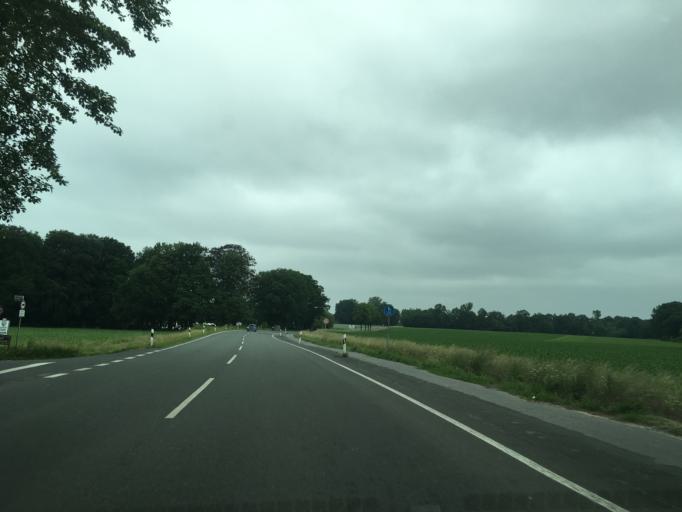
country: DE
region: North Rhine-Westphalia
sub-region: Regierungsbezirk Munster
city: Steinfurt
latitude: 52.1206
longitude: 7.3373
